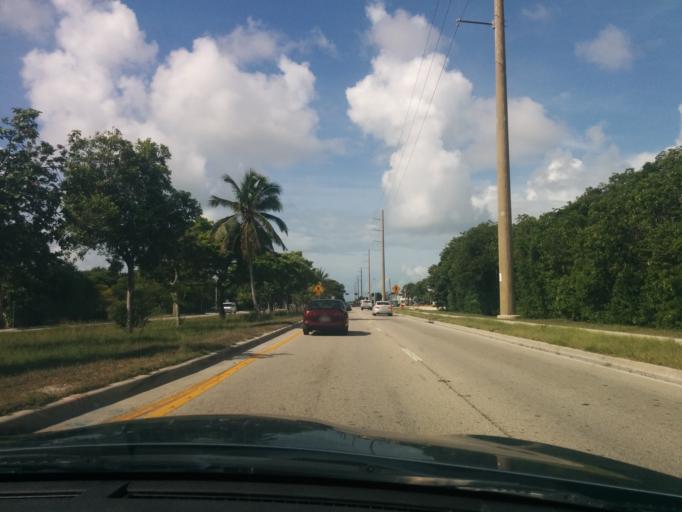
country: US
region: Florida
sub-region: Monroe County
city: Tavernier
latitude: 25.0123
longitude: -80.5143
